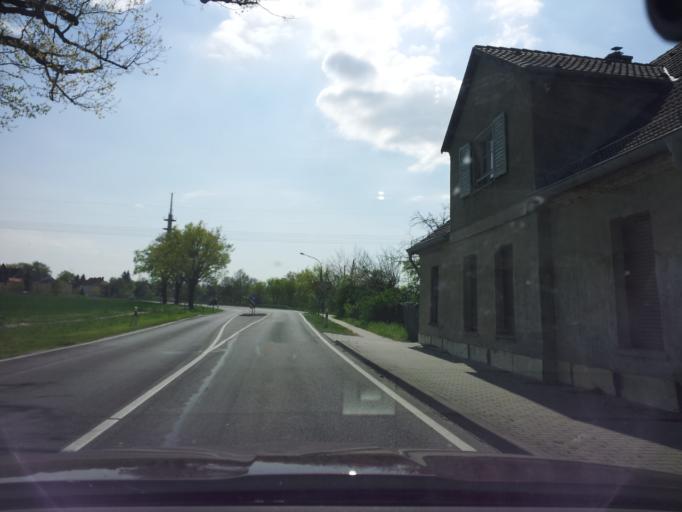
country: DE
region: Brandenburg
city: Treuenbrietzen
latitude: 52.1055
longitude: 12.8817
